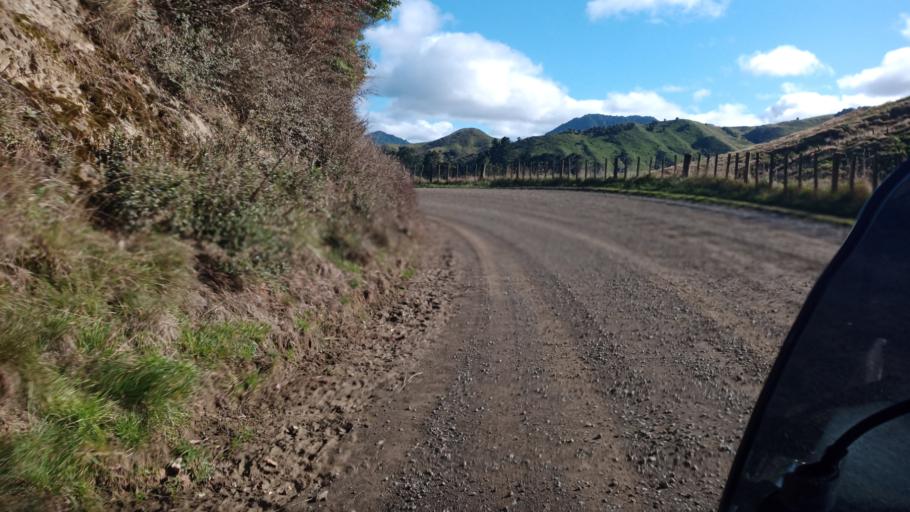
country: NZ
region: Bay of Plenty
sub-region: Opotiki District
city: Opotiki
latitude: -38.4673
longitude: 177.4289
